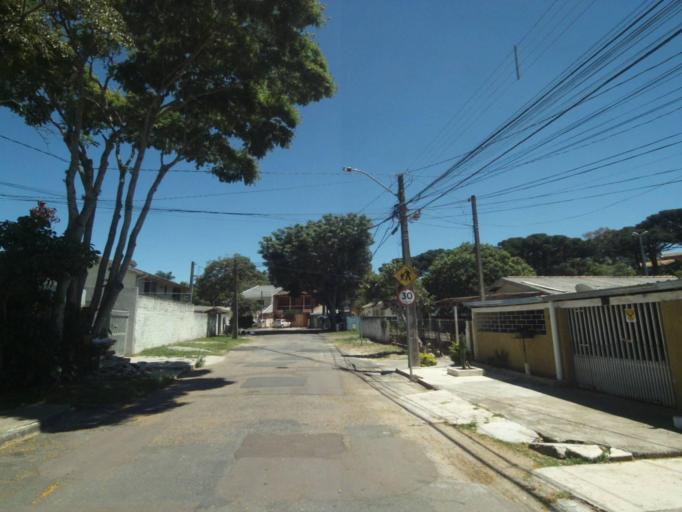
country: BR
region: Parana
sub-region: Curitiba
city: Curitiba
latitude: -25.4730
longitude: -49.3435
